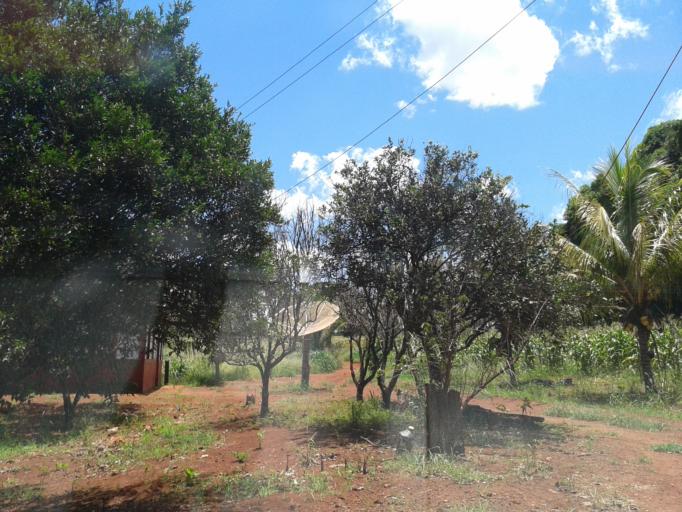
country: BR
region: Minas Gerais
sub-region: Centralina
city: Centralina
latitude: -18.7009
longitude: -49.1739
